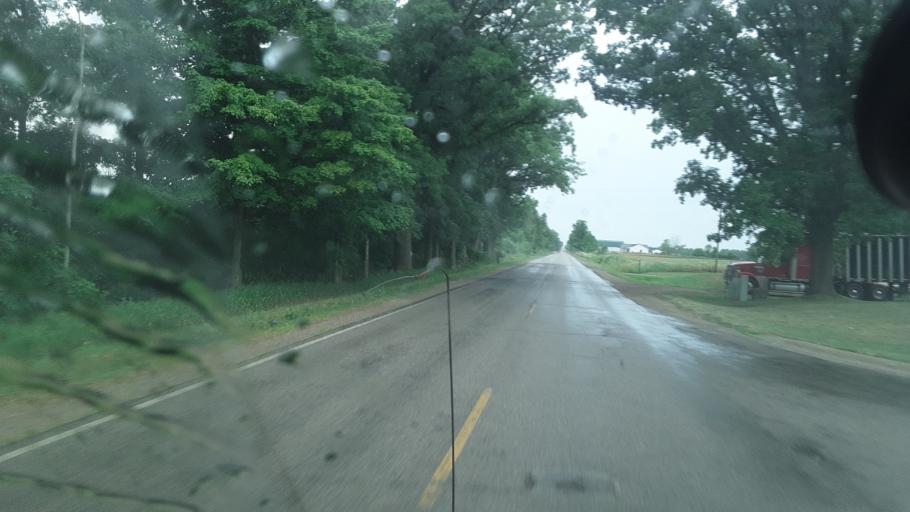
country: US
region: Michigan
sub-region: Hillsdale County
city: Reading
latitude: 41.7080
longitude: -84.7572
